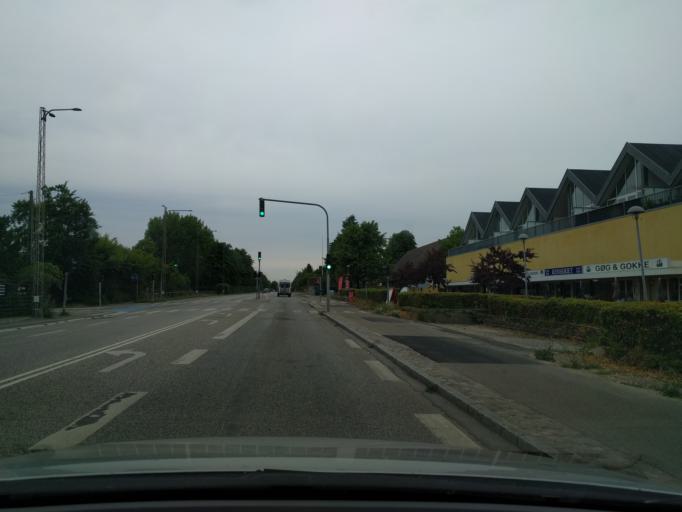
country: DK
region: Capital Region
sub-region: Dragor Kommune
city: Dragor
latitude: 55.5947
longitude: 12.6621
